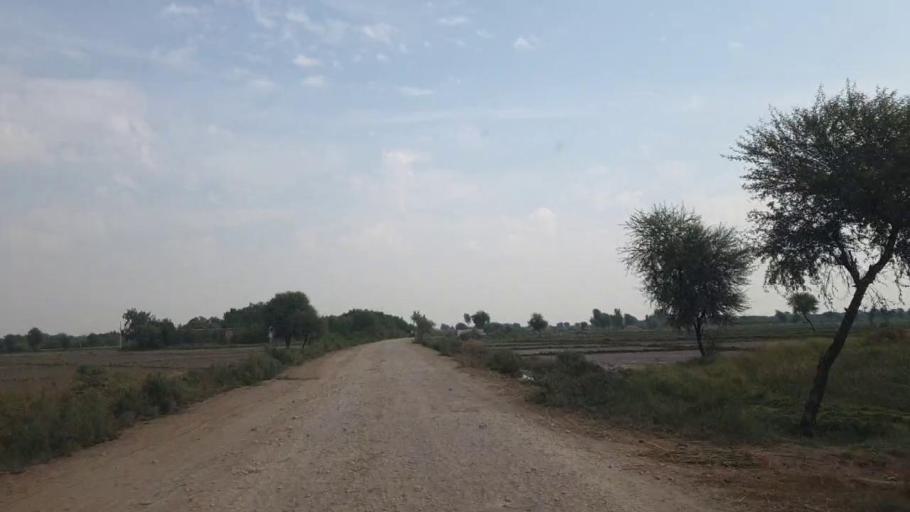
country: PK
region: Sindh
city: Rajo Khanani
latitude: 24.9587
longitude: 69.0057
